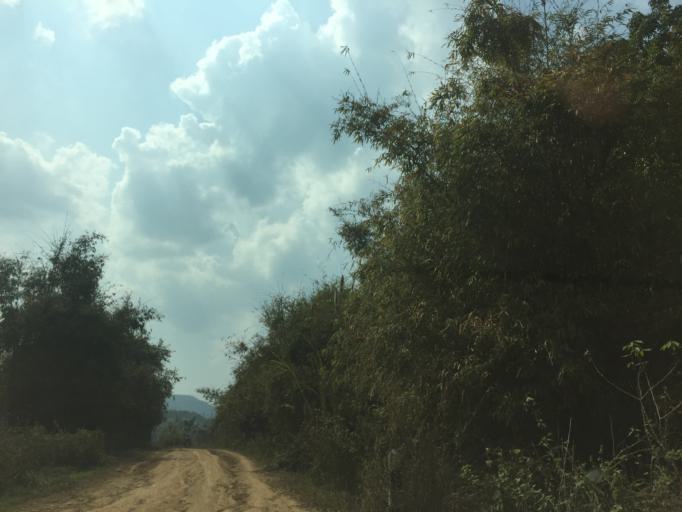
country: TH
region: Nan
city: Thung Chang
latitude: 19.7322
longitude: 100.7336
